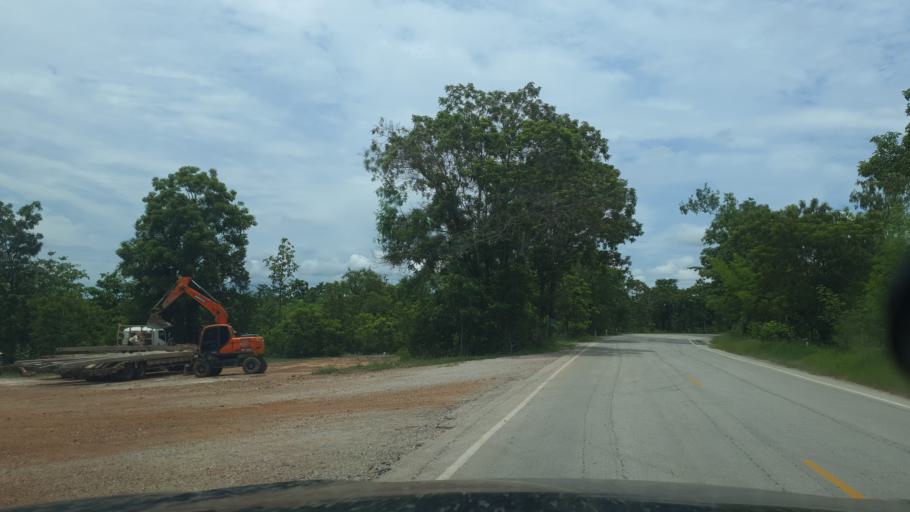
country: TH
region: Lampang
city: Sop Prap
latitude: 17.9142
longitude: 99.3982
